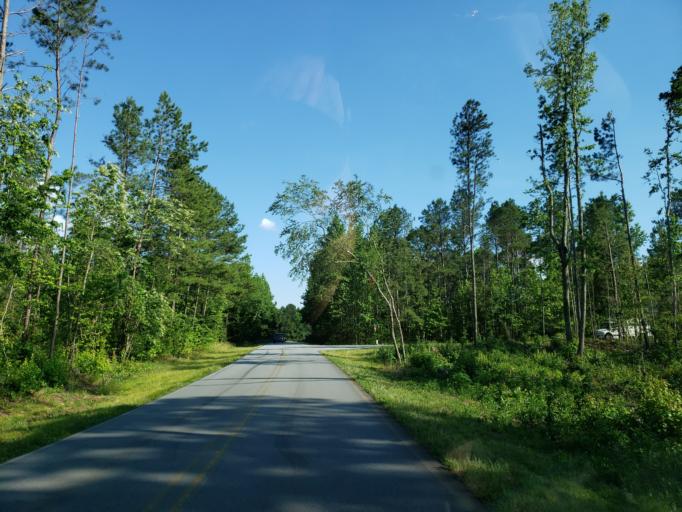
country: US
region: Georgia
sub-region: Haralson County
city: Bremen
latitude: 33.6937
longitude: -85.0985
